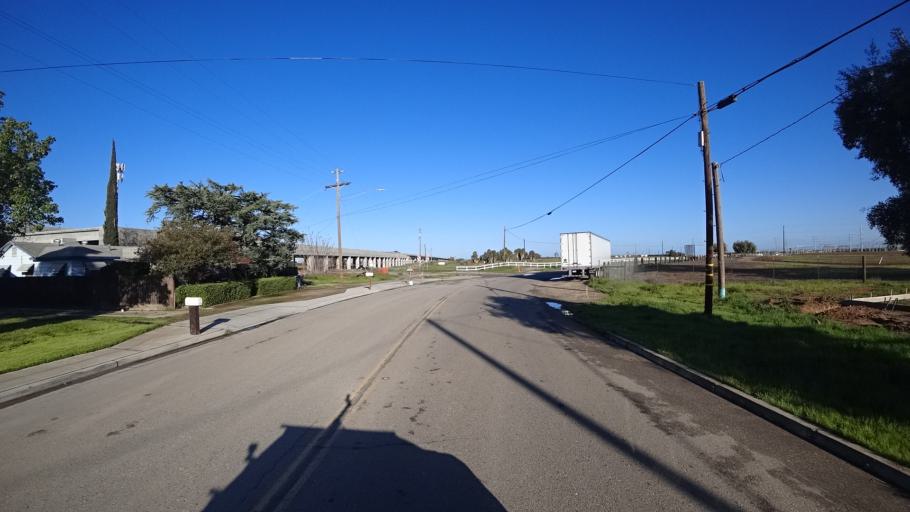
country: US
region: California
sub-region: Fresno County
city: Biola
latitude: 36.8385
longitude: -119.9212
